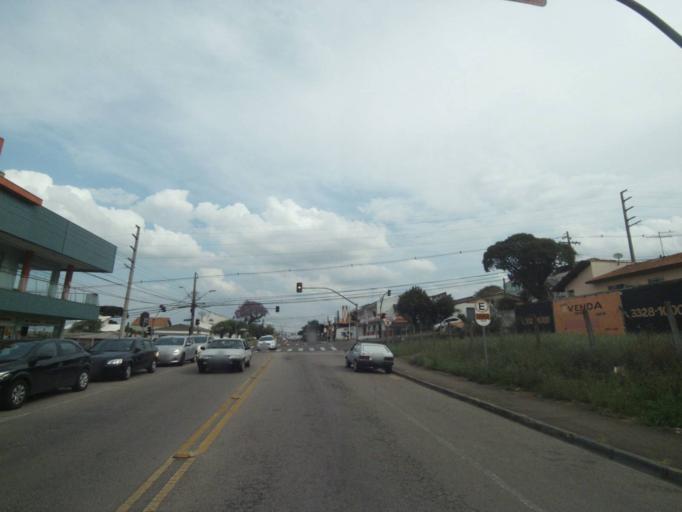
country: BR
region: Parana
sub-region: Pinhais
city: Pinhais
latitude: -25.4069
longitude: -49.2090
